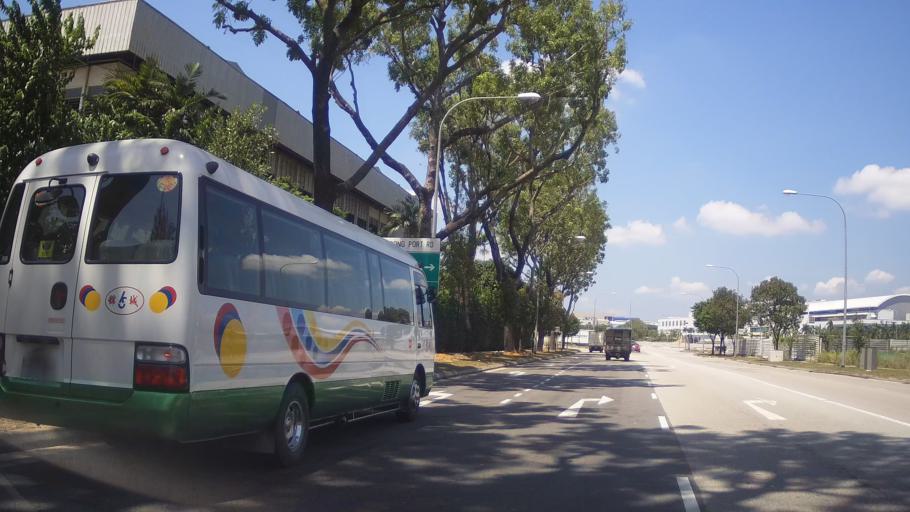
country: SG
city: Singapore
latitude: 1.3204
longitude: 103.7219
